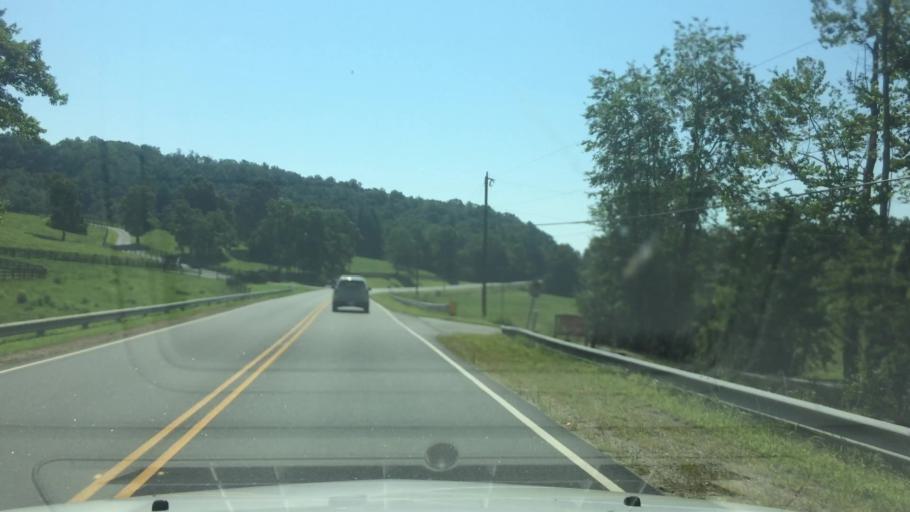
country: US
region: North Carolina
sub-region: Caldwell County
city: Hudson
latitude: 35.9155
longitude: -81.4514
